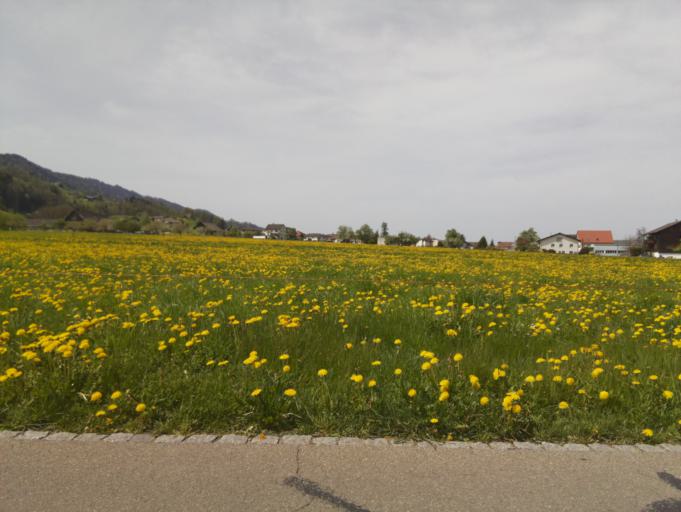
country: CH
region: Schwyz
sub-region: Bezirk March
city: Lachen
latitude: 47.1779
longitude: 8.8737
